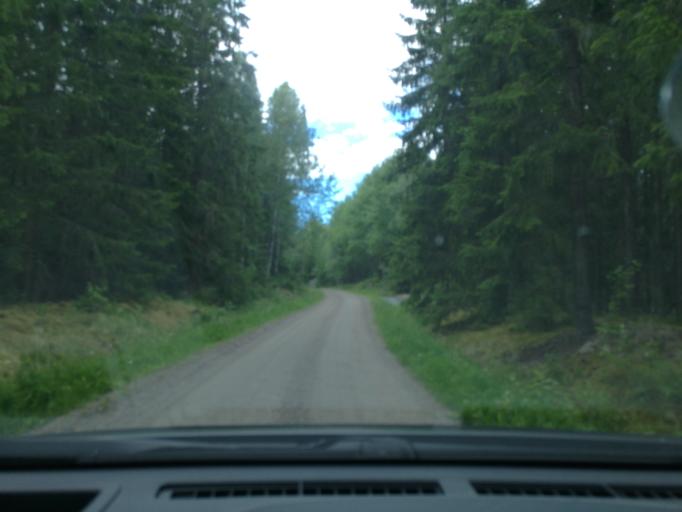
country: SE
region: Vaestmanland
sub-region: Surahammars Kommun
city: Ramnas
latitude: 59.8124
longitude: 16.3173
